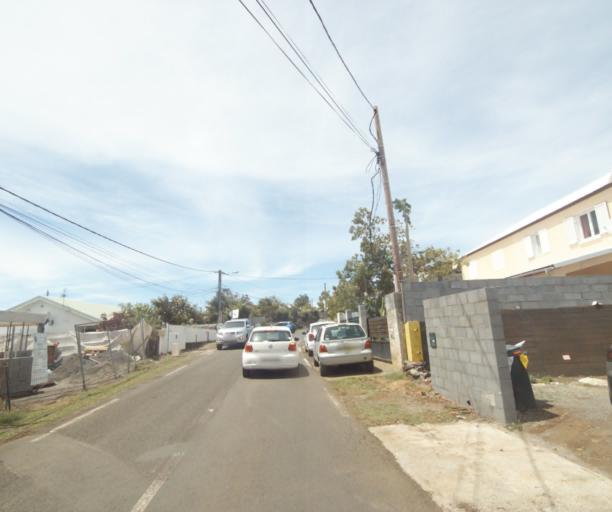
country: RE
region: Reunion
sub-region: Reunion
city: Saint-Paul
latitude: -21.0447
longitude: 55.2806
